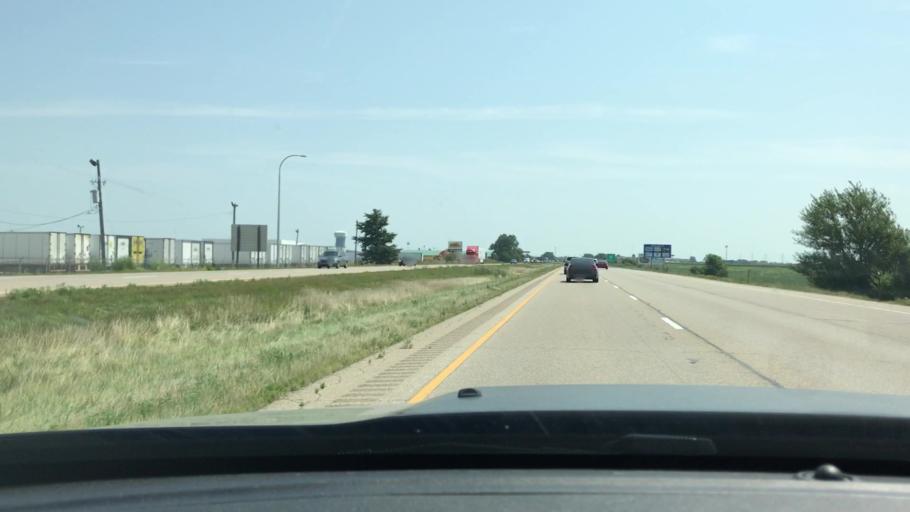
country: US
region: Illinois
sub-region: LaSalle County
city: Peru
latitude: 41.3648
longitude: -89.1479
